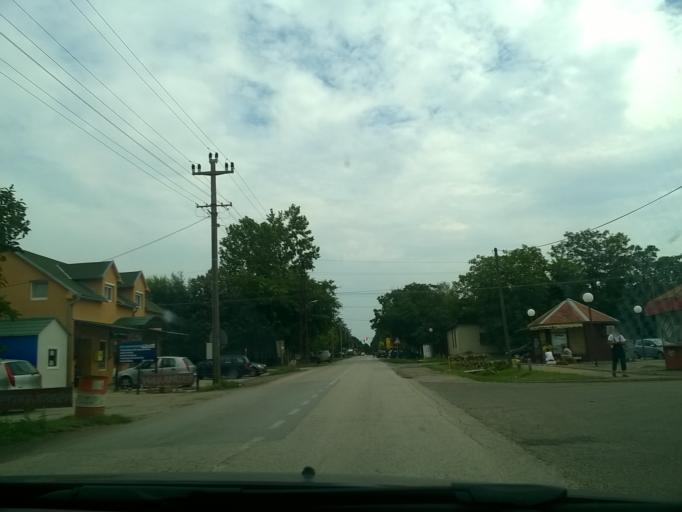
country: RS
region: Autonomna Pokrajina Vojvodina
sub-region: Srednjebanatski Okrug
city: Secanj
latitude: 45.3668
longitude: 20.7700
